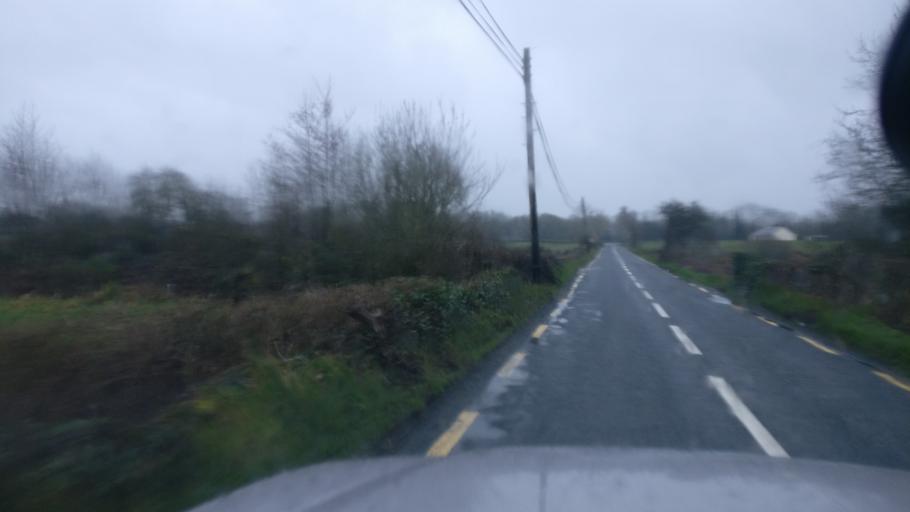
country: IE
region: Connaught
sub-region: County Galway
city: Ballinasloe
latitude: 53.2273
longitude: -8.1924
